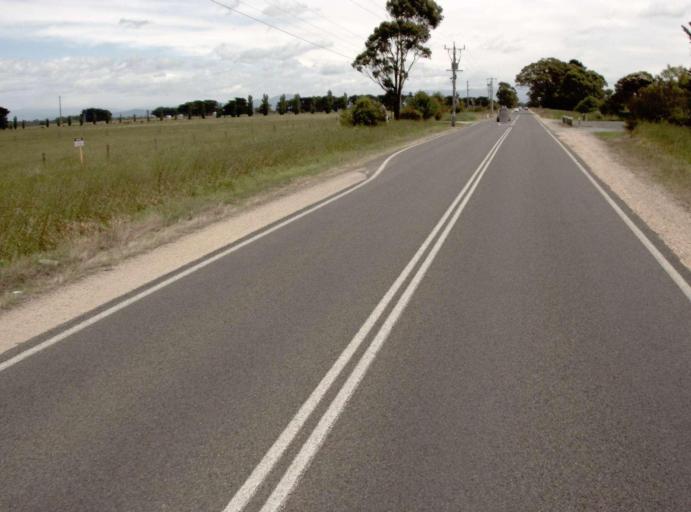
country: AU
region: Victoria
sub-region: Wellington
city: Sale
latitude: -38.0242
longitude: 147.0122
